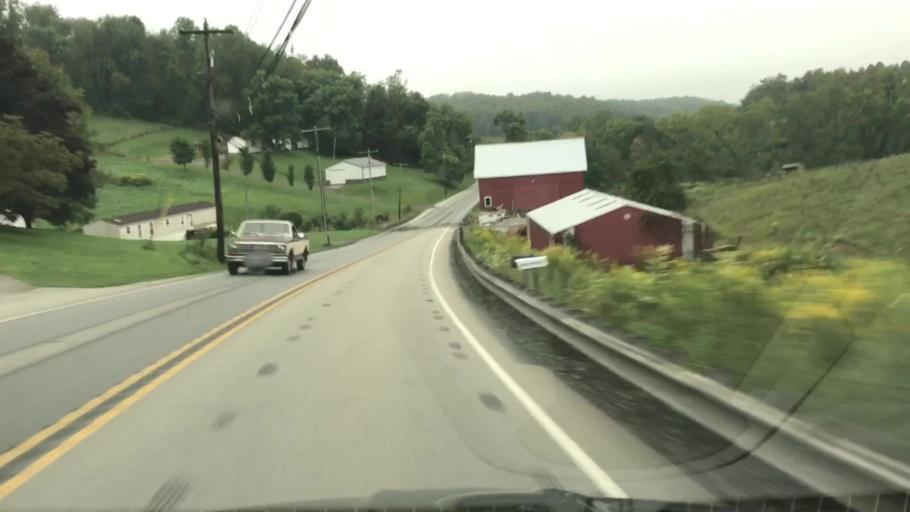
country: US
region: Pennsylvania
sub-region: Washington County
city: McMurray
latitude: 40.1796
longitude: -80.1081
